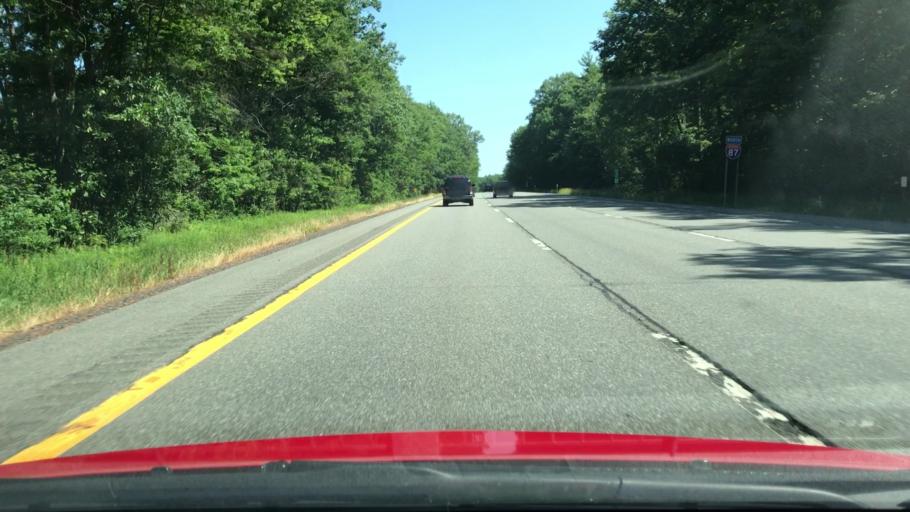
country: US
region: New York
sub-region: Warren County
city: West Glens Falls
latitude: 43.1932
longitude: -73.7023
